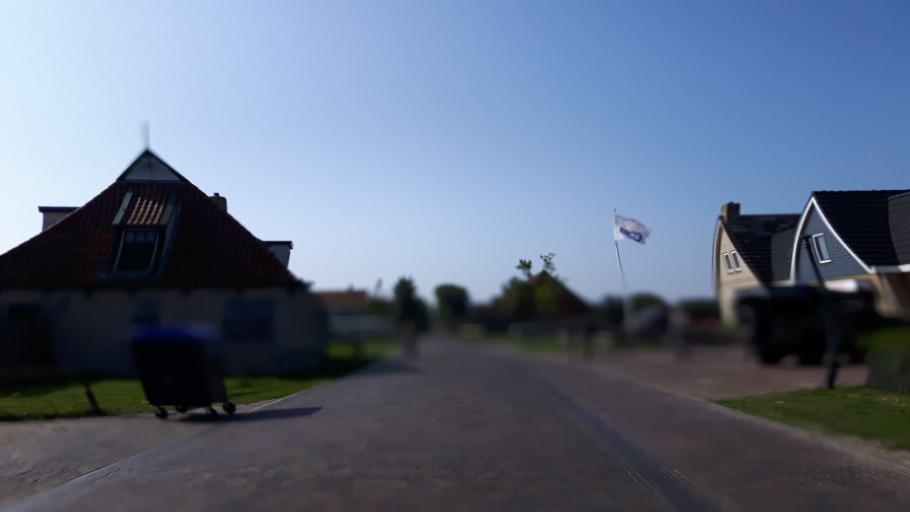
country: NL
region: Friesland
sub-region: Gemeente Ameland
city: Nes
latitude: 53.4510
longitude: 5.8011
